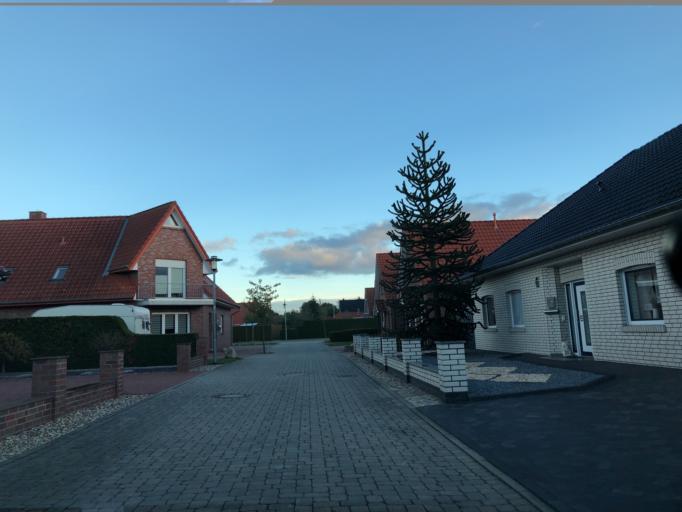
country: DE
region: Lower Saxony
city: Papenburg
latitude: 53.0844
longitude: 7.4218
